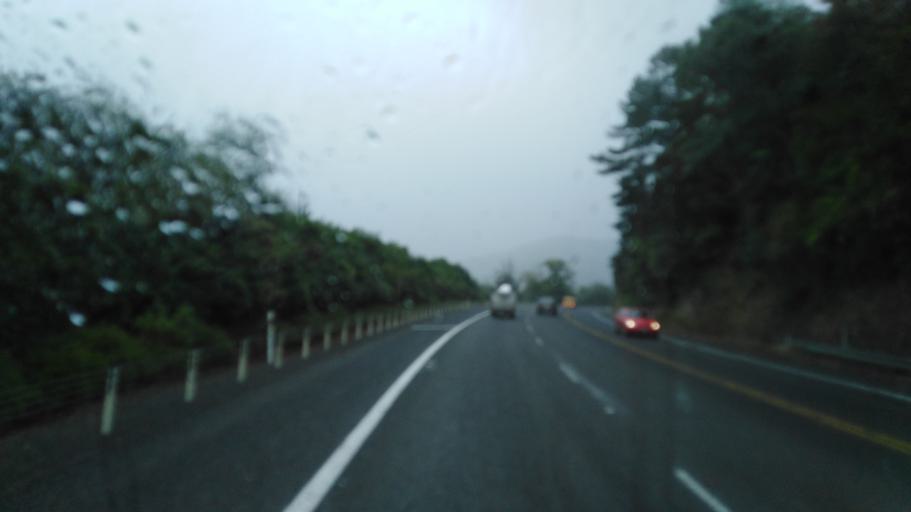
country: NZ
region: Marlborough
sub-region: Marlborough District
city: Picton
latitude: -41.3801
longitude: 173.9474
